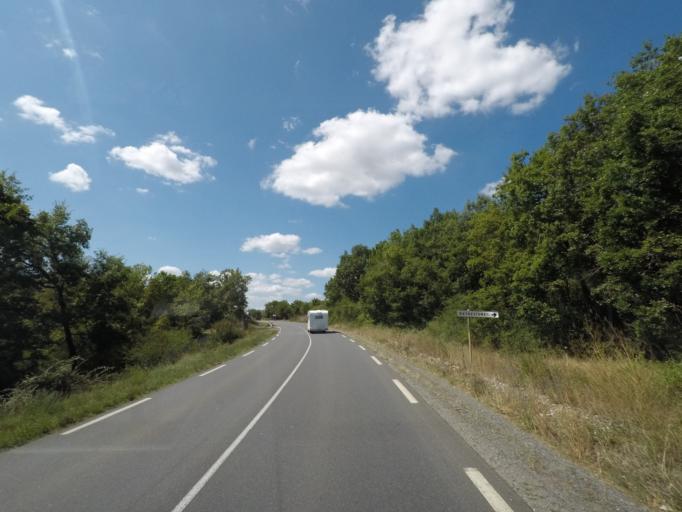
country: FR
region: Midi-Pyrenees
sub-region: Departement du Lot
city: Lacapelle-Marival
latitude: 44.6226
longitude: 1.9134
